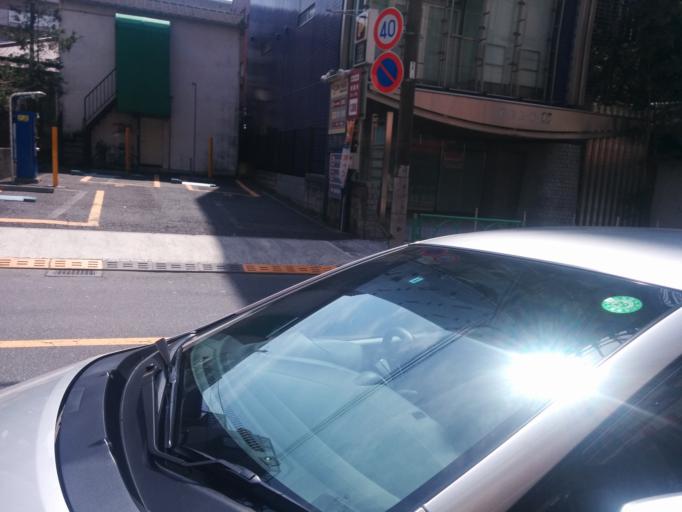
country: JP
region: Tokyo
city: Tokyo
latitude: 35.6911
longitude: 139.6706
